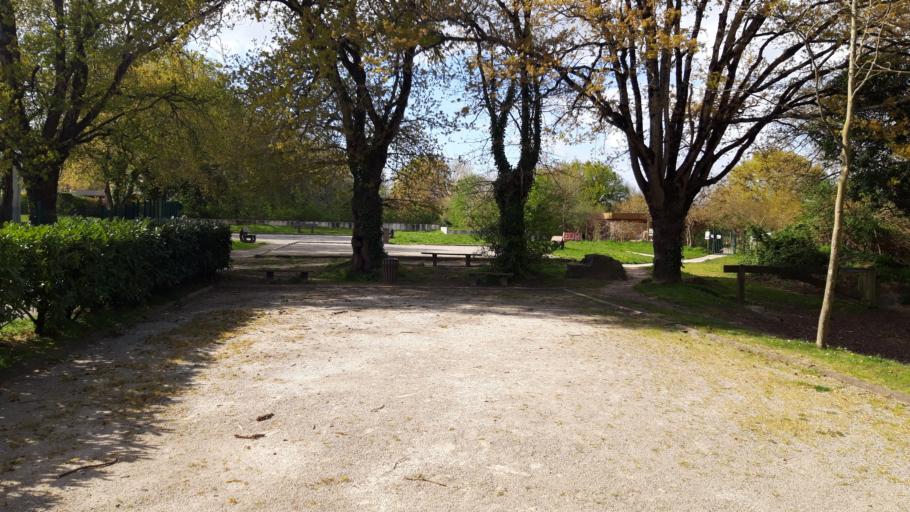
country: FR
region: Pays de la Loire
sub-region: Departement de la Loire-Atlantique
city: Orvault
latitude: 47.2312
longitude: -1.6054
